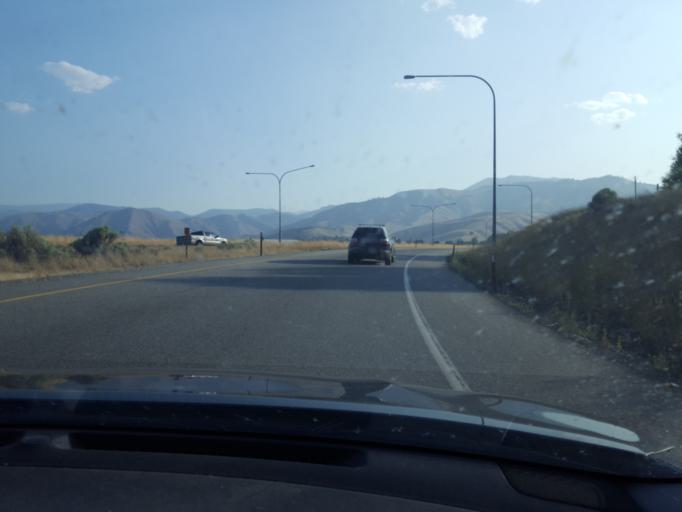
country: US
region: Washington
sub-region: Chelan County
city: Sunnyslope
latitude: 47.4726
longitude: -120.3267
